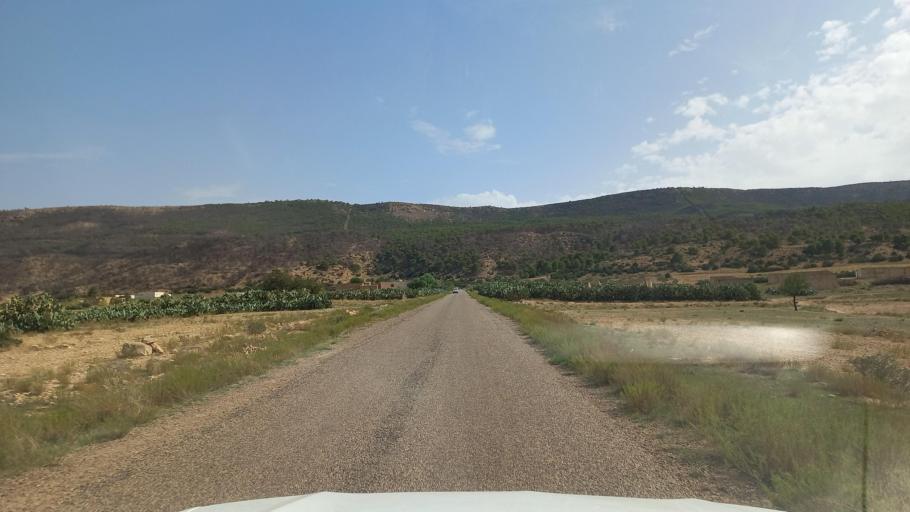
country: TN
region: Al Qasrayn
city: Kasserine
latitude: 35.3567
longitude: 8.8867
